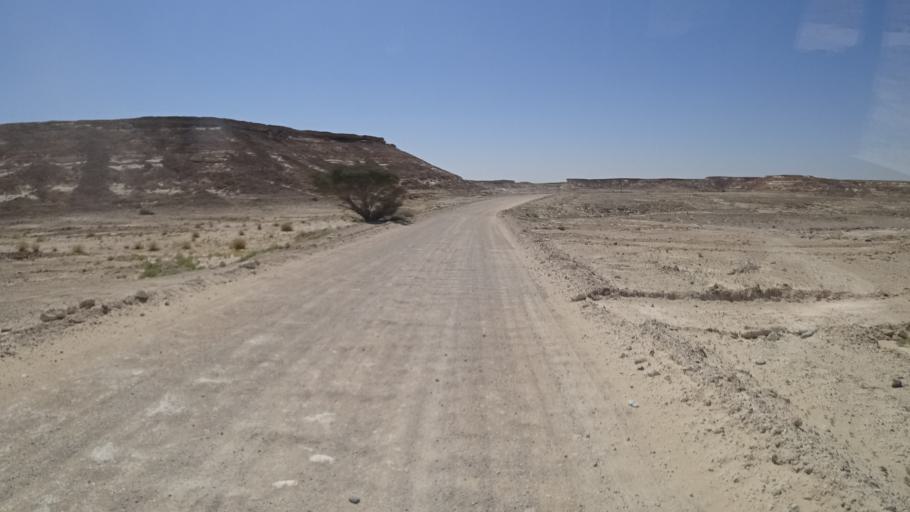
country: OM
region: Zufar
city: Salalah
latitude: 17.4664
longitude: 53.3417
